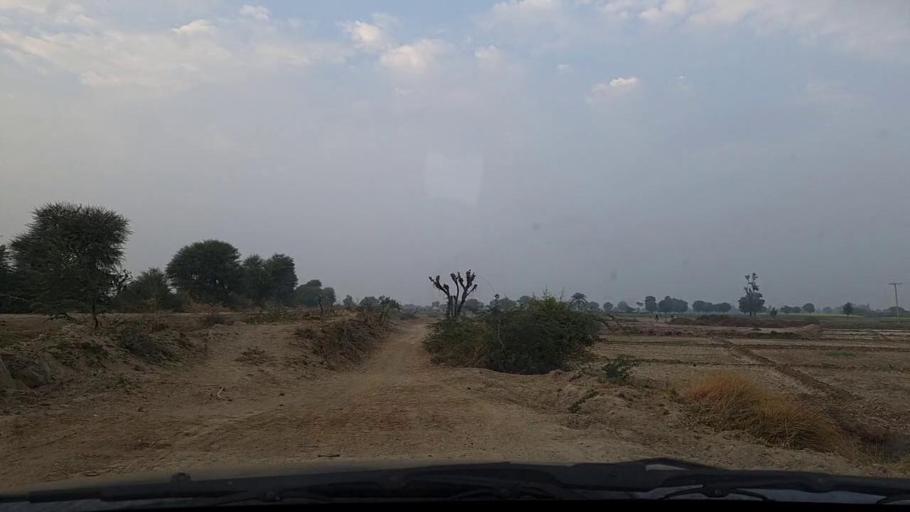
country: PK
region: Sindh
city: Pithoro
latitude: 25.6028
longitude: 69.4589
